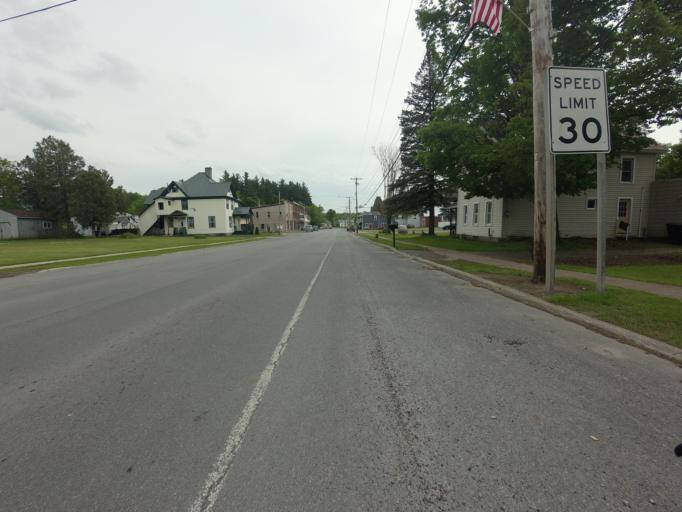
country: US
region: New York
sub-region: St. Lawrence County
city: Gouverneur
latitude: 44.3257
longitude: -75.2505
